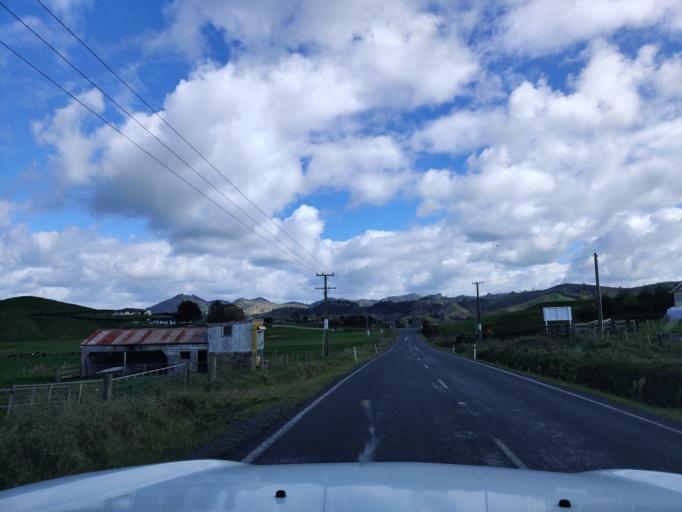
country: NZ
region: Waikato
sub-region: Waikato District
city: Ngaruawahia
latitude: -37.5769
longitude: 175.2333
